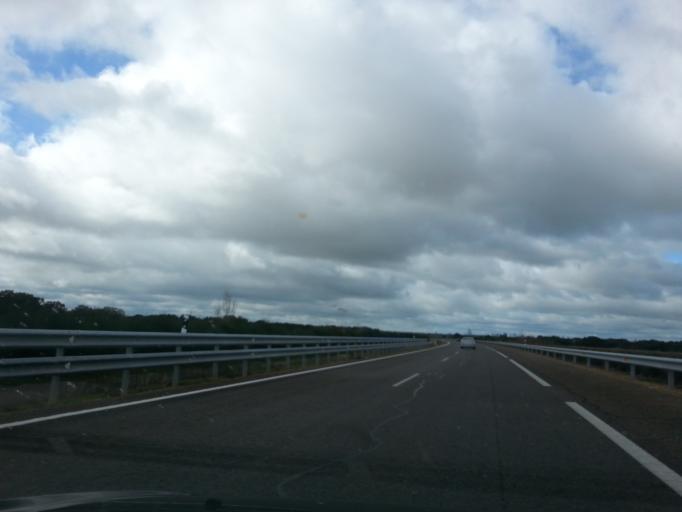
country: ES
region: Castille and Leon
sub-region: Provincia de Salamanca
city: La Fuente de San Esteban
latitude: 40.8034
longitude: -6.1999
